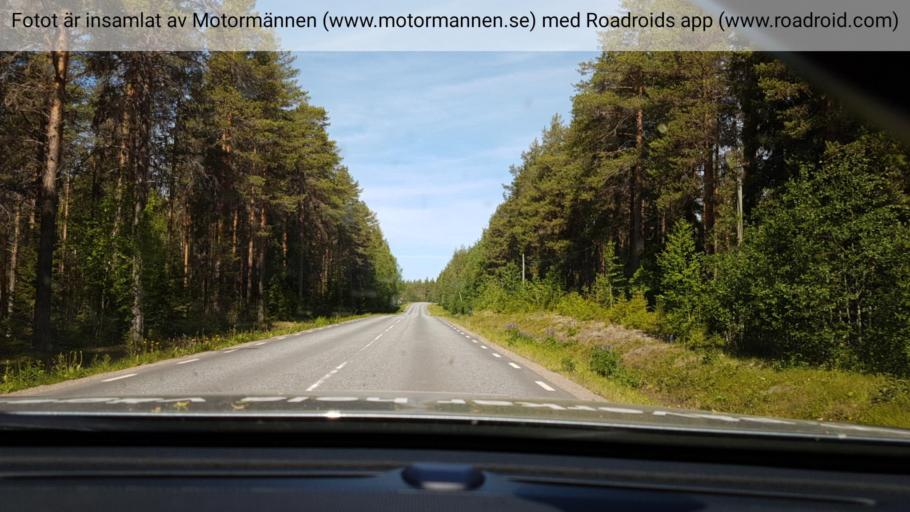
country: SE
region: Vaesterbotten
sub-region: Dorotea Kommun
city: Dorotea
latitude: 64.2635
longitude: 16.3631
